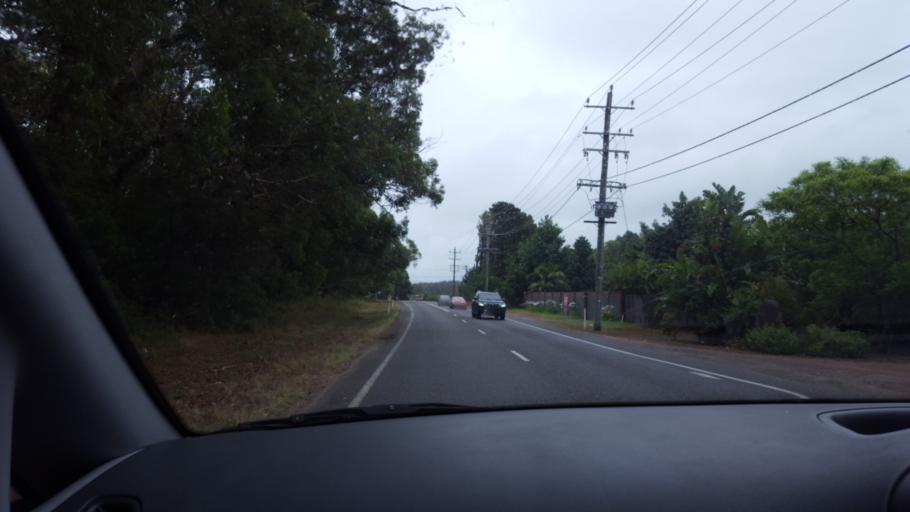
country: AU
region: New South Wales
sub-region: Port Stephens Shire
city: Anna Bay
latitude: -32.7716
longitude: 152.0760
